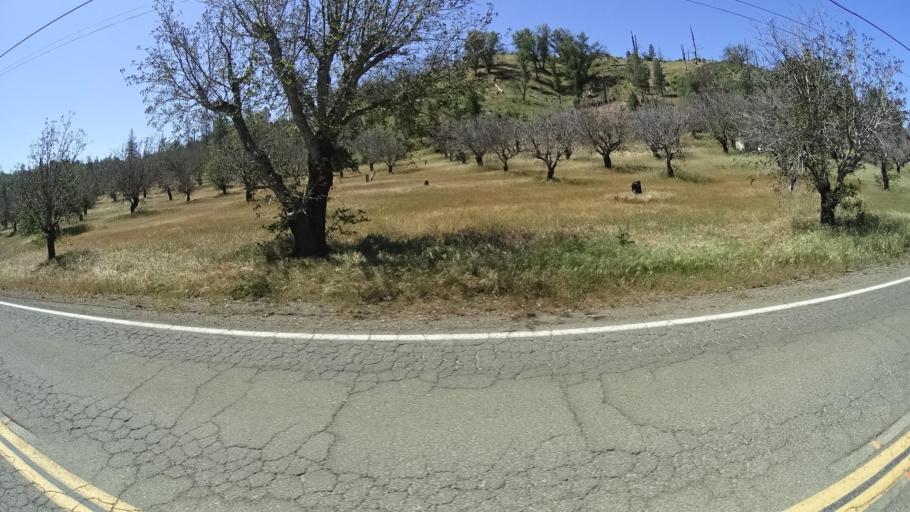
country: US
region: California
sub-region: Lake County
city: Lower Lake
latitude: 38.9085
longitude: -122.5876
